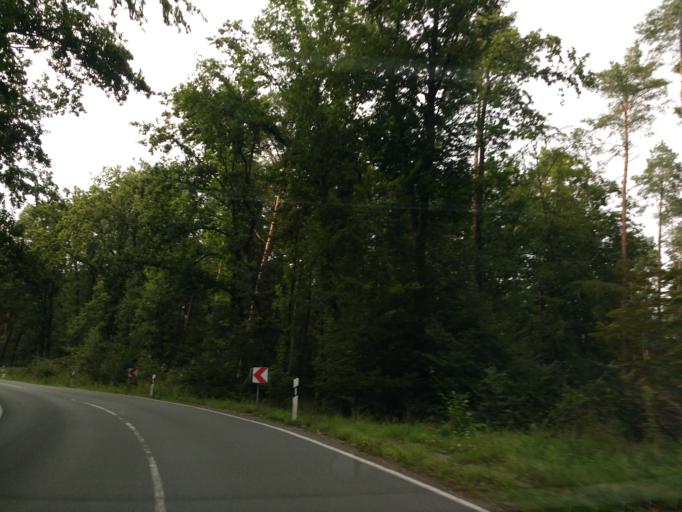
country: DE
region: North Rhine-Westphalia
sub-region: Regierungsbezirk Detmold
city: Lage
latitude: 51.9332
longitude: 8.8045
